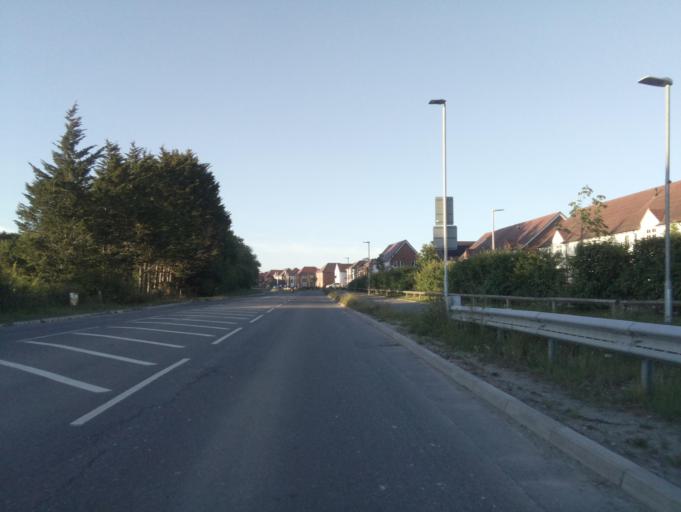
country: GB
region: England
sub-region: Devon
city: Newton Abbot
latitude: 50.5515
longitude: -3.6086
